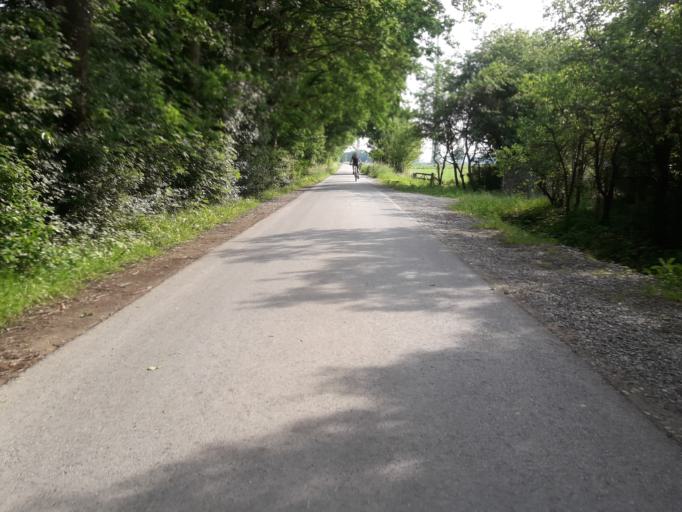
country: DE
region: North Rhine-Westphalia
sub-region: Regierungsbezirk Detmold
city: Salzkotten
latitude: 51.7078
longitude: 8.6593
